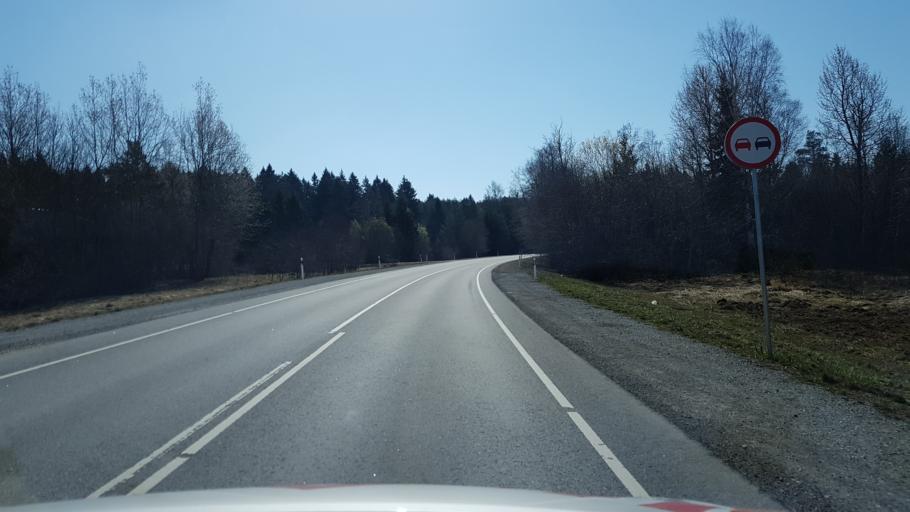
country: EE
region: Ida-Virumaa
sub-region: Kohtla-Jaerve linn
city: Kohtla-Jarve
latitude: 59.3355
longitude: 27.2629
